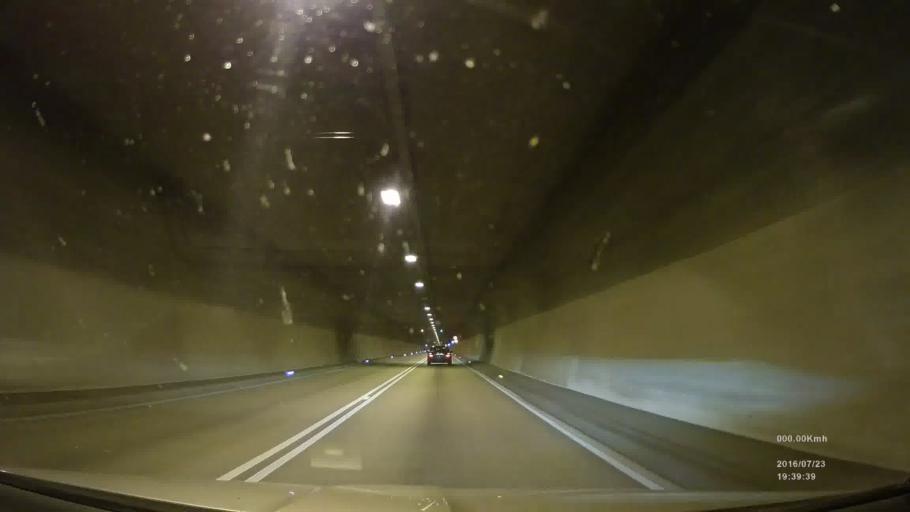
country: SK
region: Kosicky
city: Krompachy
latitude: 49.0057
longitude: 20.8664
